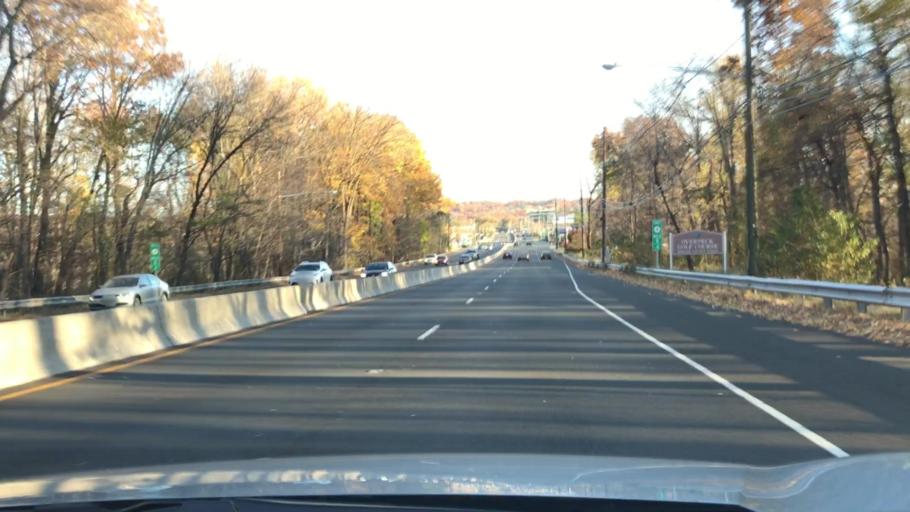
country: US
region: New Jersey
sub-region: Bergen County
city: Englewood
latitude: 40.8853
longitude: -73.9915
